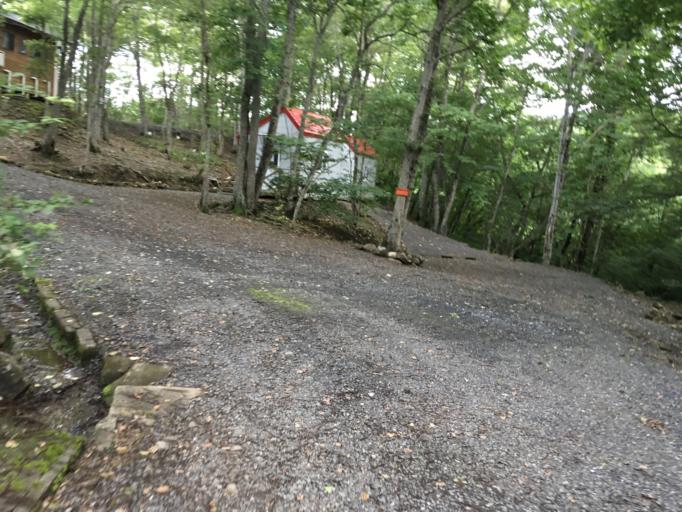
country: JP
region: Iwate
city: Ichinoseki
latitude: 38.9906
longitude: 140.9814
